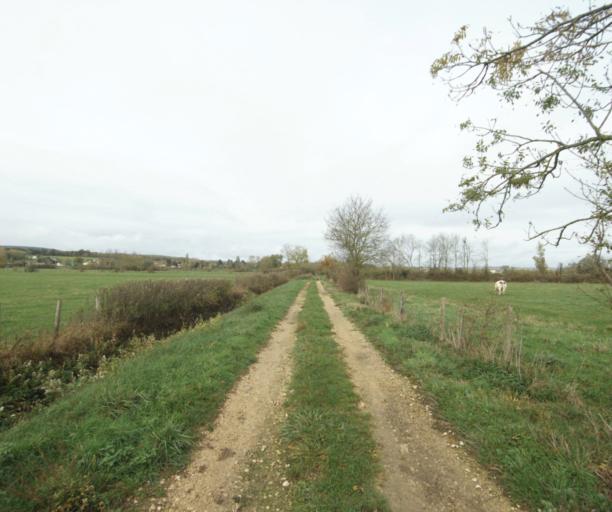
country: FR
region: Rhone-Alpes
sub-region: Departement de l'Ain
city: Pont-de-Vaux
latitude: 46.4518
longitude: 4.8945
